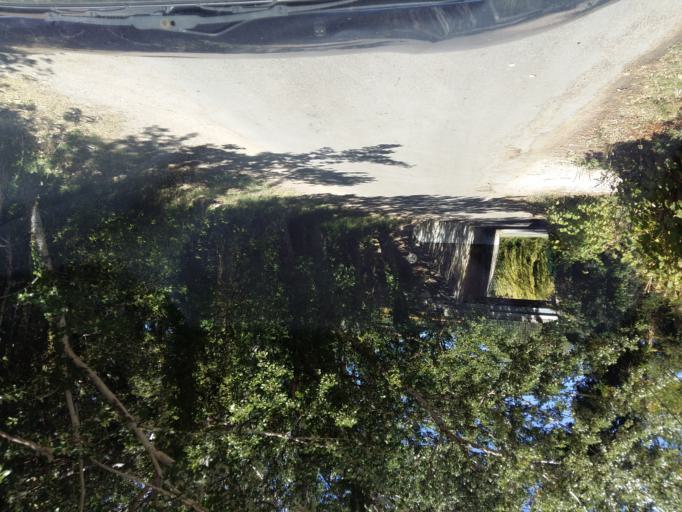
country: FR
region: Provence-Alpes-Cote d'Azur
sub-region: Departement du Vaucluse
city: Loriol-du-Comtat
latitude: 44.0876
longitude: 5.0117
